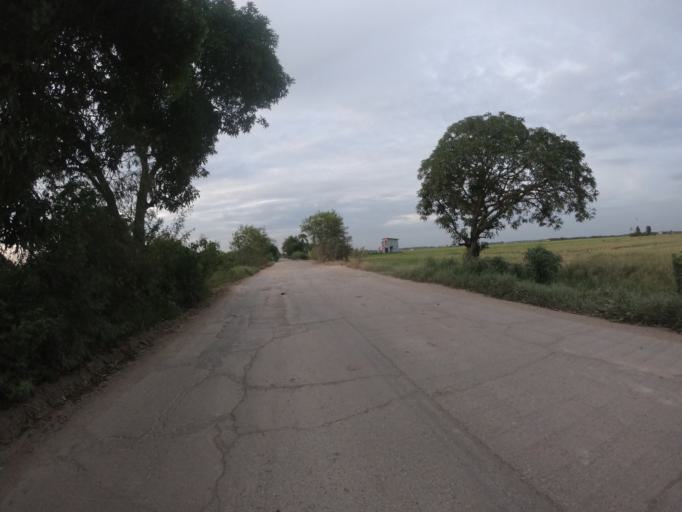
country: TH
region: Pathum Thani
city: Ban Lam Luk Ka
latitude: 14.0014
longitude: 100.8001
